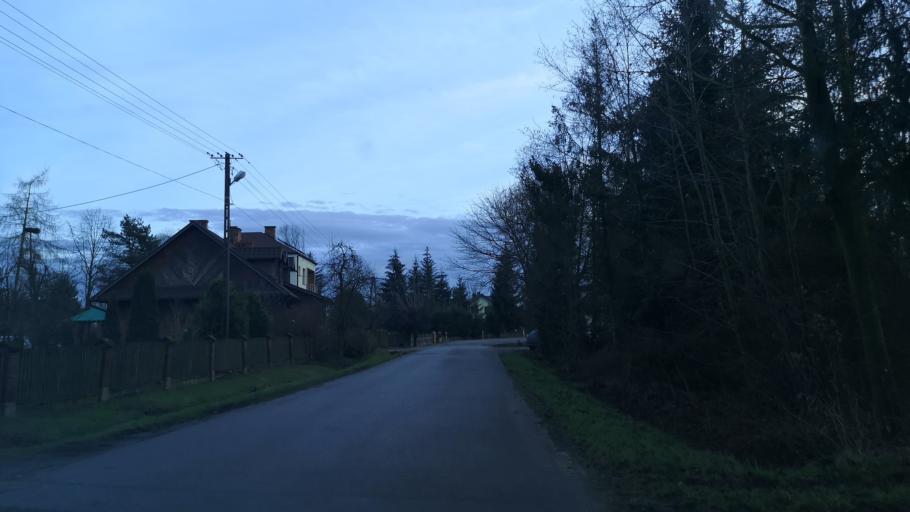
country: PL
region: Subcarpathian Voivodeship
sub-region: Powiat lezajski
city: Piskorowice
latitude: 50.2601
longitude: 22.5966
